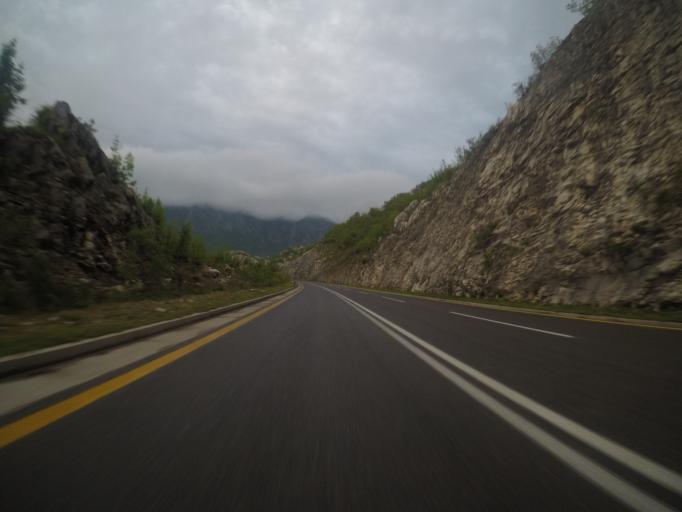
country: ME
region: Bar
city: Sutomore
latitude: 42.2128
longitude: 19.0481
